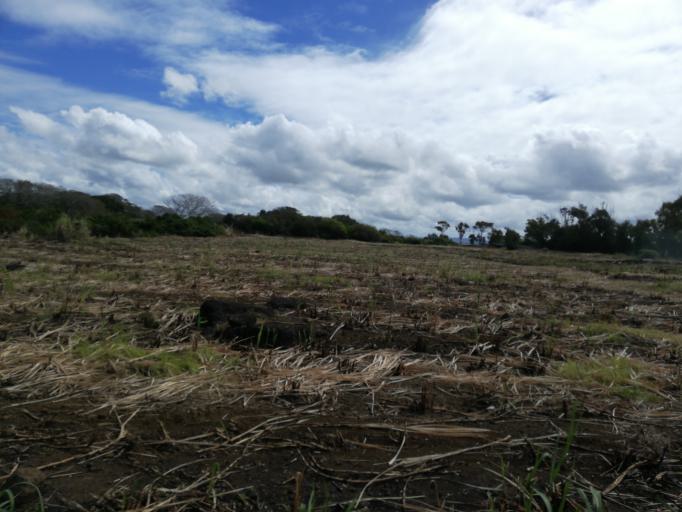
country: MU
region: Grand Port
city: Plaine Magnien
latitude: -20.4645
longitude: 57.6774
